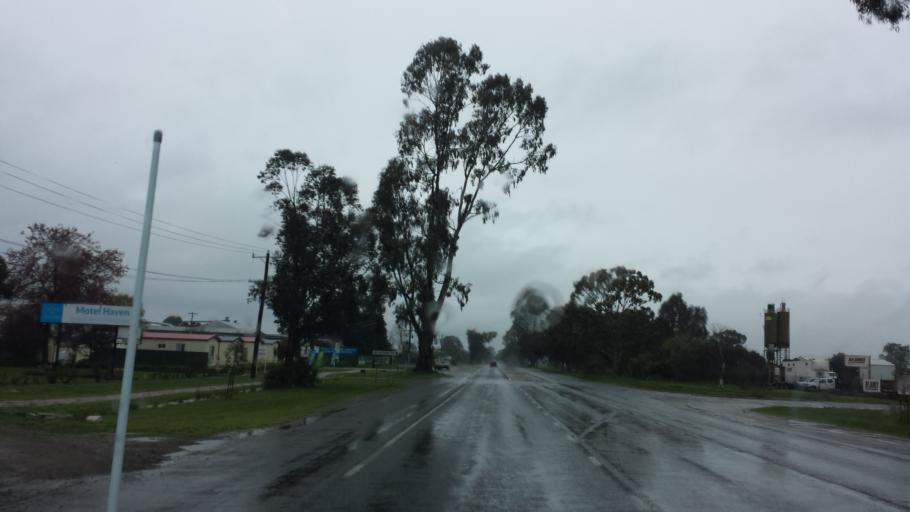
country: AU
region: Victoria
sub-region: Benalla
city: Benalla
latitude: -36.5443
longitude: 146.0074
